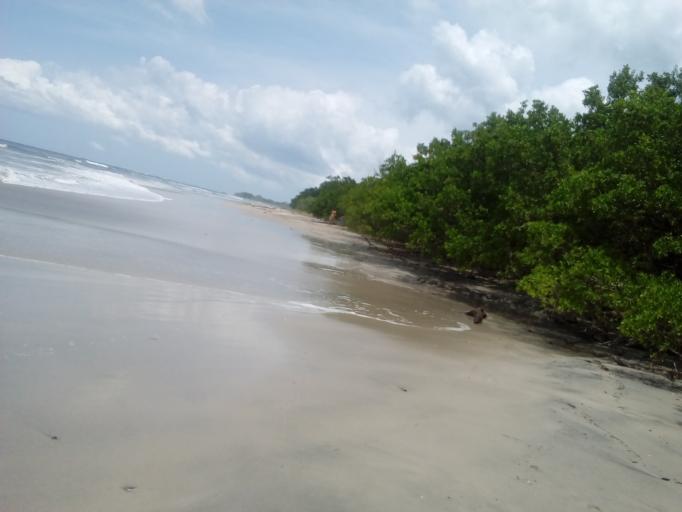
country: CR
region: Guanacaste
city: Samara
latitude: 9.9327
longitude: -85.6640
